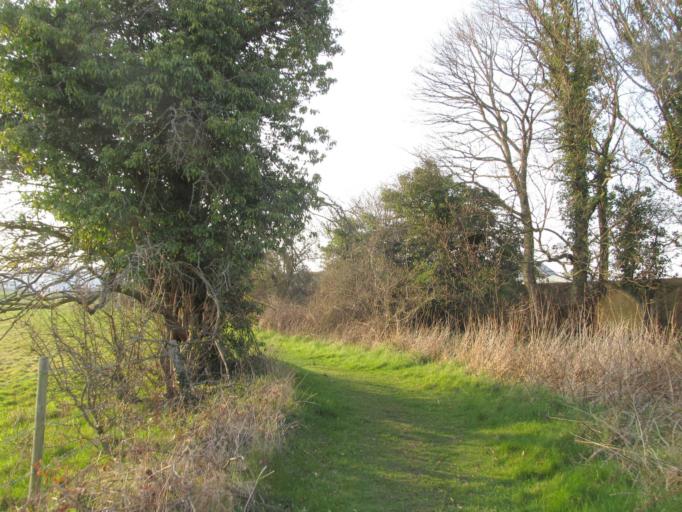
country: GB
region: Wales
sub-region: County of Flintshire
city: Buckley
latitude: 53.2009
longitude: -3.0901
